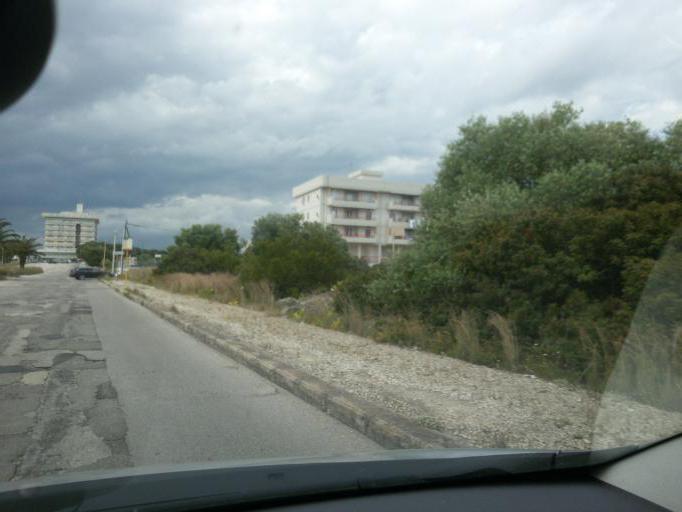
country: IT
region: Apulia
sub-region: Provincia di Taranto
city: Paolo VI
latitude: 40.5348
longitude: 17.2770
